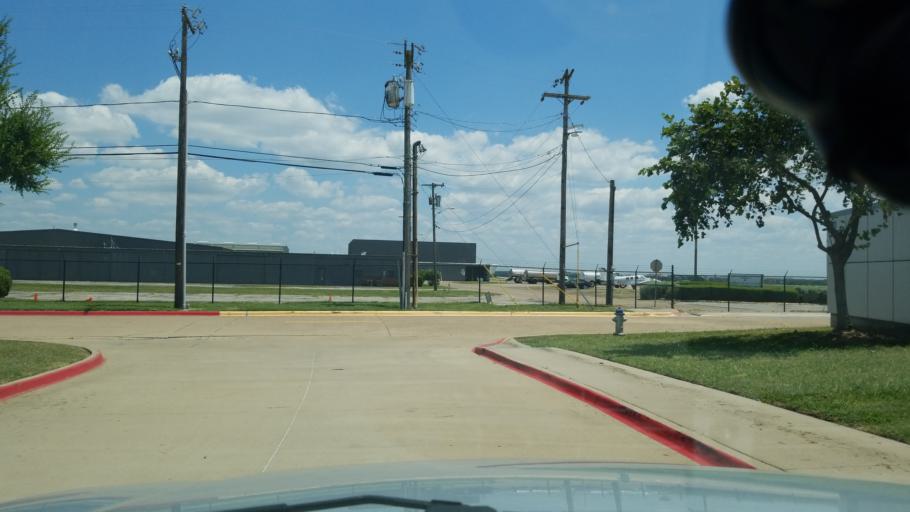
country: US
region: Texas
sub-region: Dallas County
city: Duncanville
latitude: 32.6807
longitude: -96.8644
